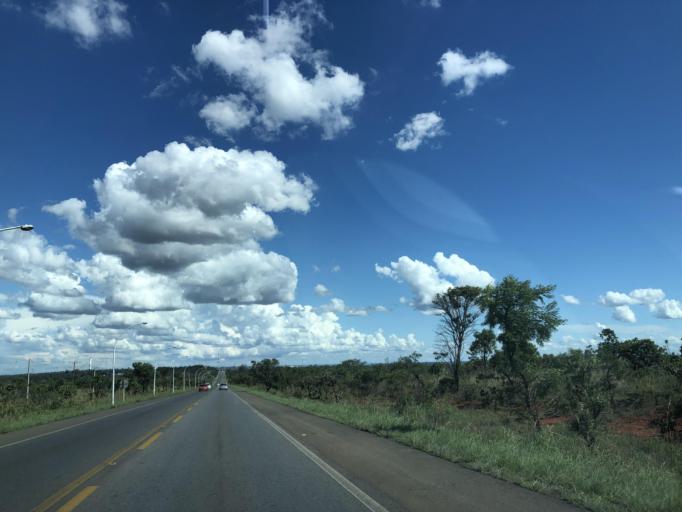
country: BR
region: Federal District
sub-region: Brasilia
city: Brasilia
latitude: -15.6729
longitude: -47.8777
